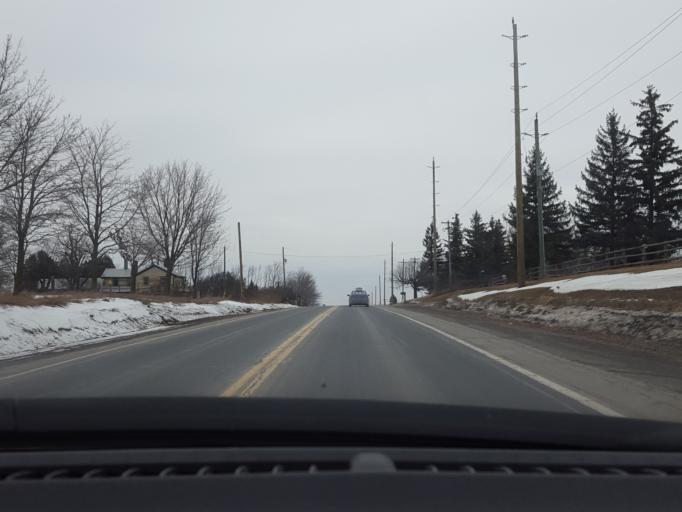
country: CA
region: Ontario
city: Newmarket
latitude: 44.1489
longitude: -79.4272
